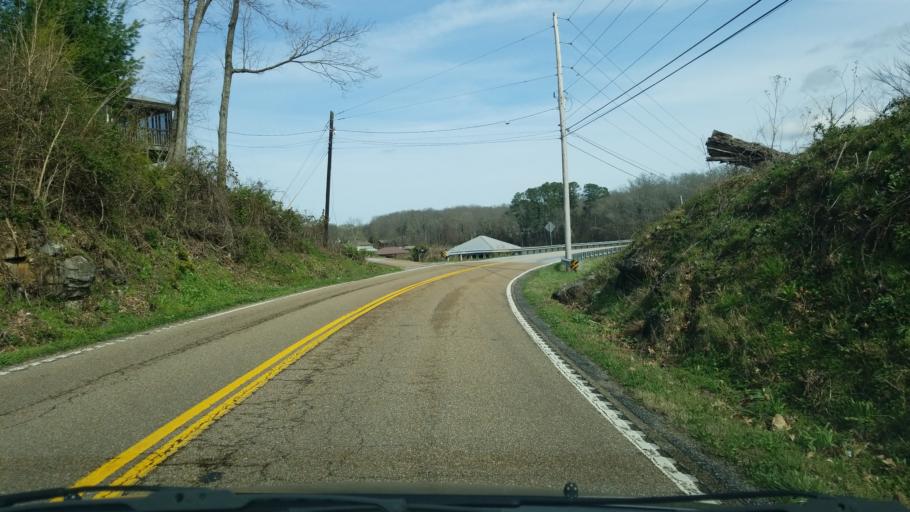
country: US
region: Tennessee
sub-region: Hamilton County
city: Lakesite
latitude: 35.1561
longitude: -85.0617
